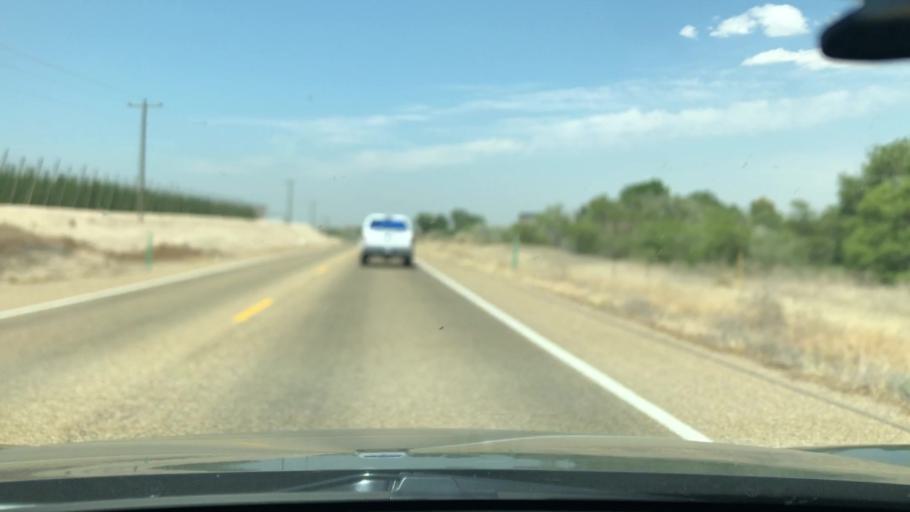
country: US
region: Idaho
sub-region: Canyon County
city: Wilder
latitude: 43.7093
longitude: -116.9119
